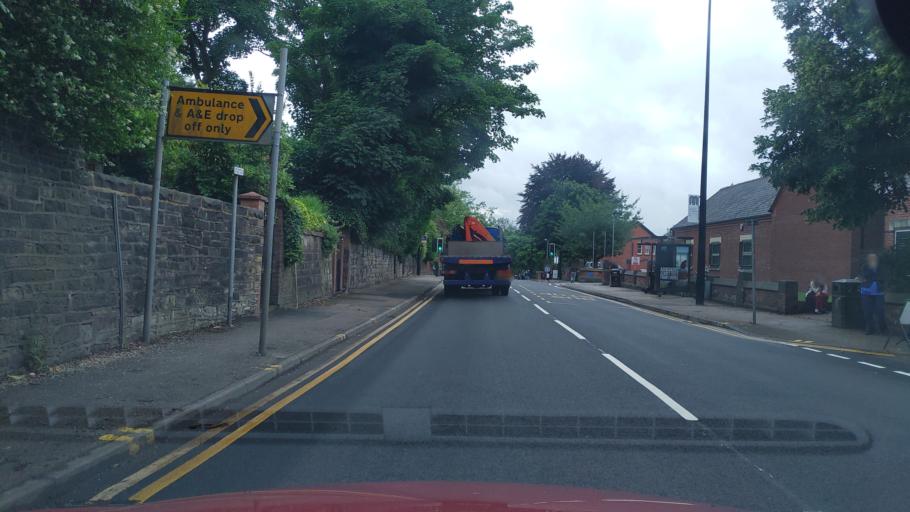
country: GB
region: England
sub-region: Borough of Wigan
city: Ince-in-Makerfield
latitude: 53.5580
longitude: -2.6282
